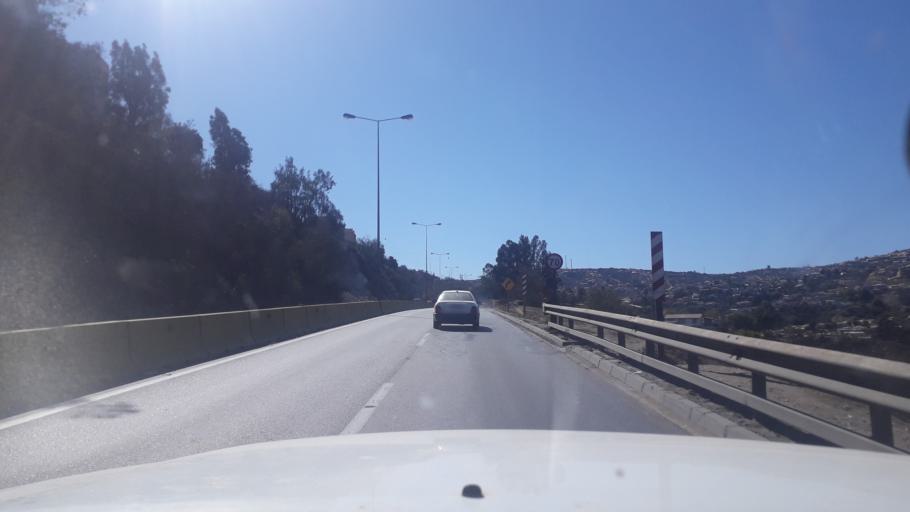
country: CL
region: Valparaiso
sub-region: Provincia de Valparaiso
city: Vina del Mar
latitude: -33.0338
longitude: -71.5011
